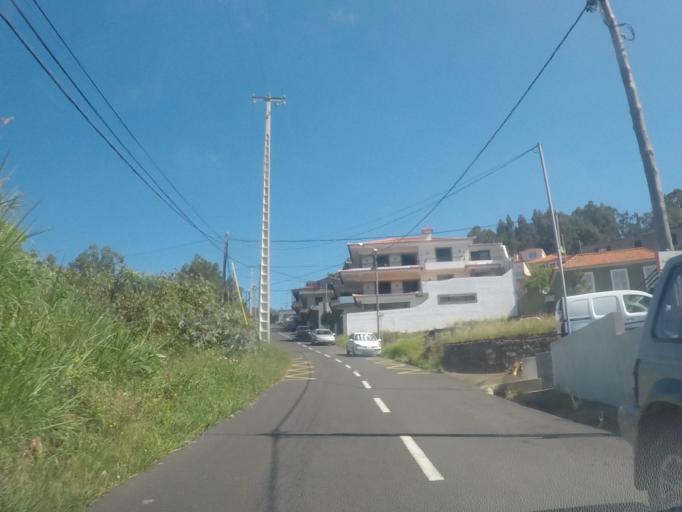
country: PT
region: Madeira
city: Camara de Lobos
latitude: 32.6759
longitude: -16.9651
